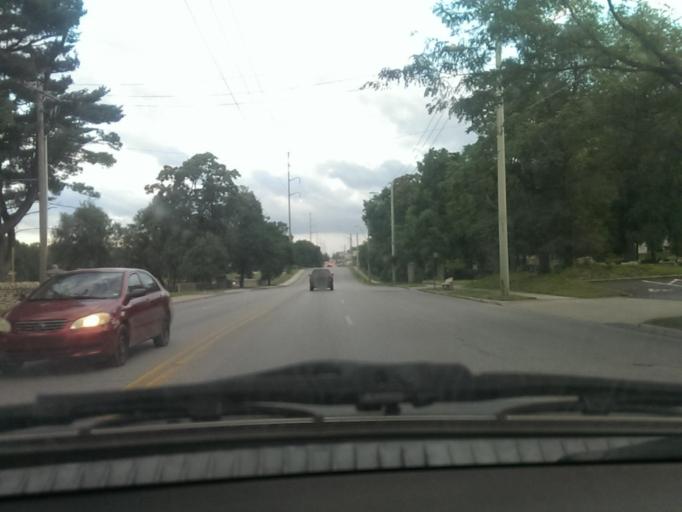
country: US
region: Kansas
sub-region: Johnson County
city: Mission Hills
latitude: 39.0031
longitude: -94.5752
